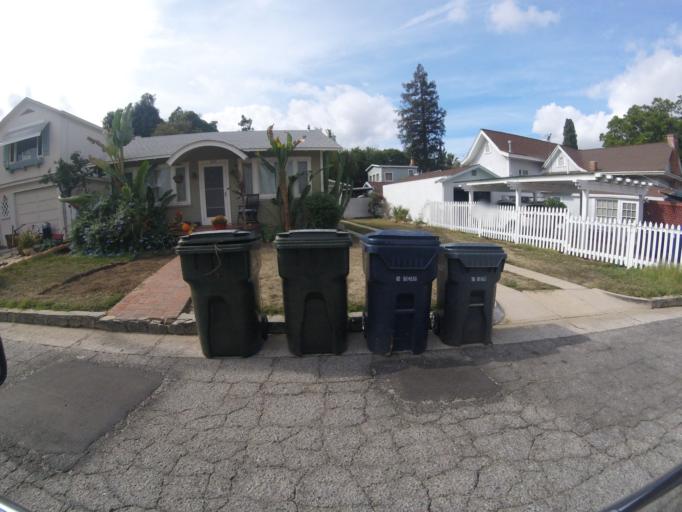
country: US
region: California
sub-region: San Bernardino County
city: Redlands
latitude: 34.0474
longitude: -117.1744
